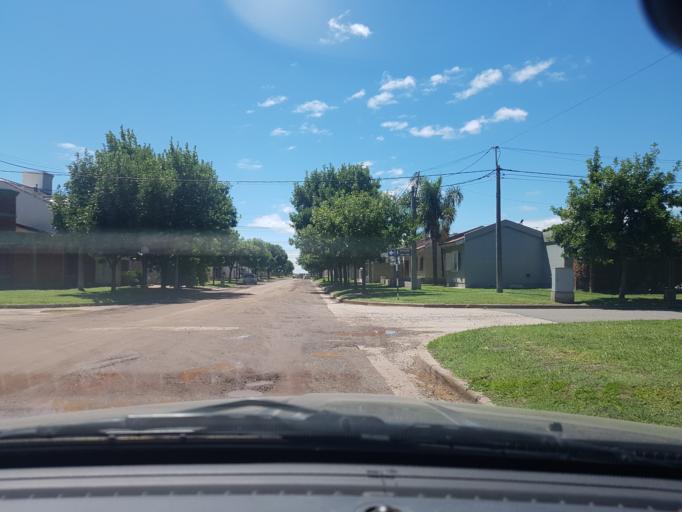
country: AR
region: Cordoba
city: Las Perdices
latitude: -32.7577
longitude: -63.7768
